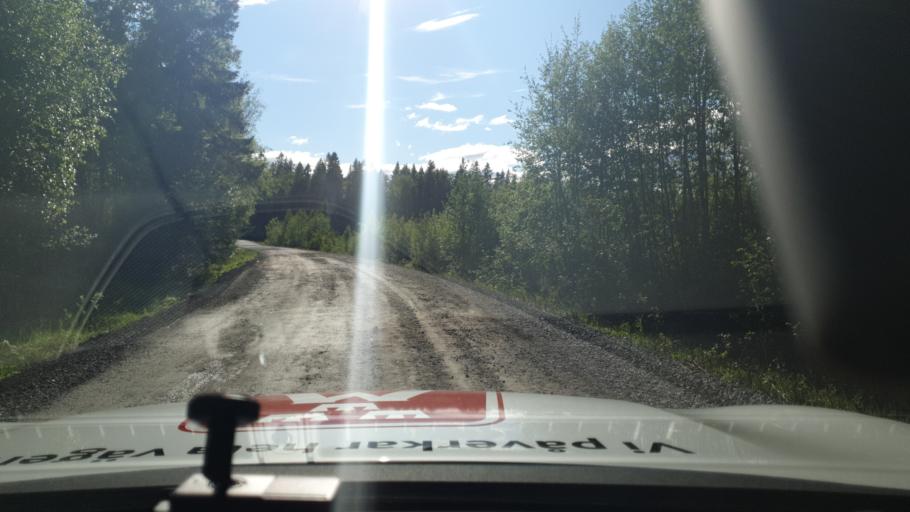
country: SE
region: Vaesterbotten
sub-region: Umea Kommun
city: Taftea
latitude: 63.7684
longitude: 20.4456
